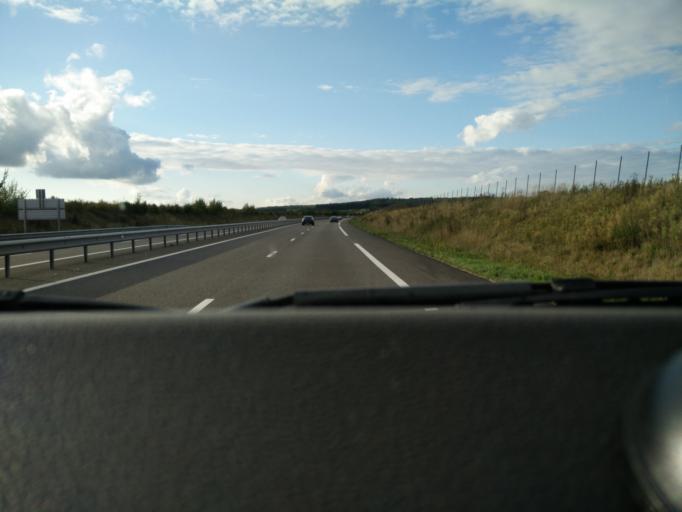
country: FR
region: Lorraine
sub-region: Departement de Meurthe-et-Moselle
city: Baccarat
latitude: 48.4824
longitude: 6.7122
